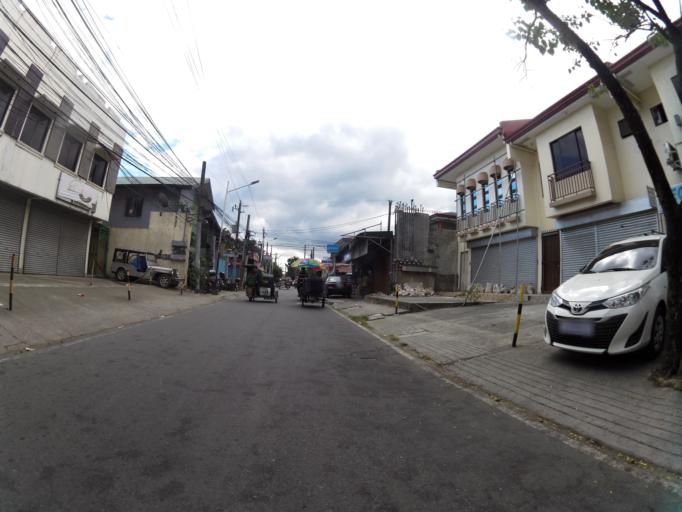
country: PH
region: Calabarzon
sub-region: Province of Rizal
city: Antipolo
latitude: 14.6297
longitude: 121.1081
